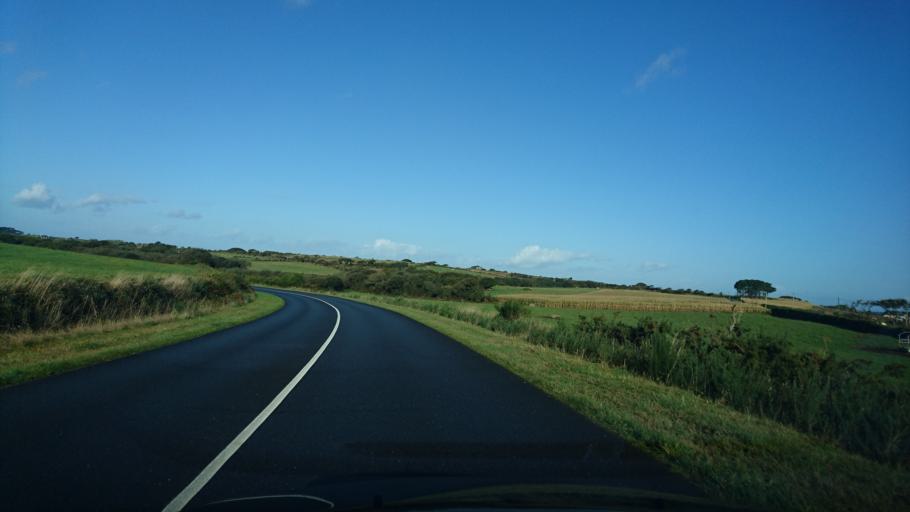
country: FR
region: Brittany
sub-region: Departement du Finistere
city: Plouarzel
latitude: 48.4378
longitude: -4.7168
